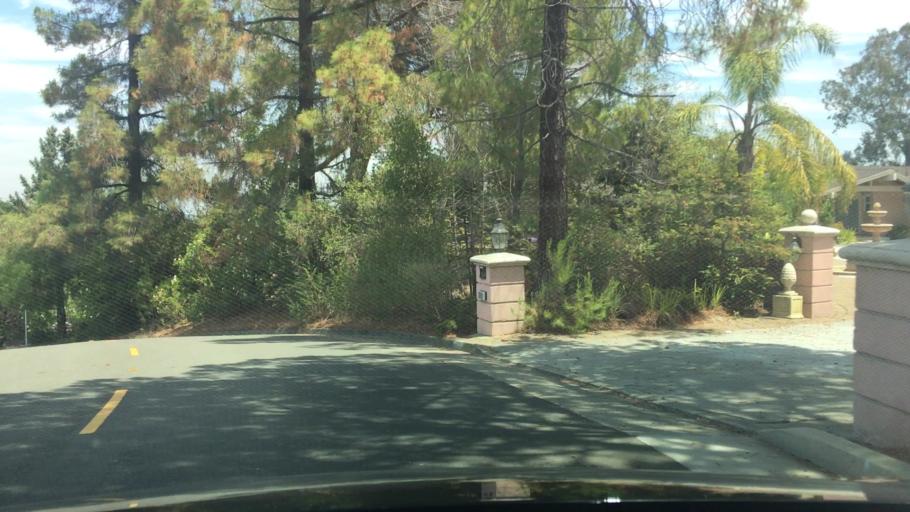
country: US
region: California
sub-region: Santa Clara County
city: Los Altos Hills
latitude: 37.3726
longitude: -122.1712
